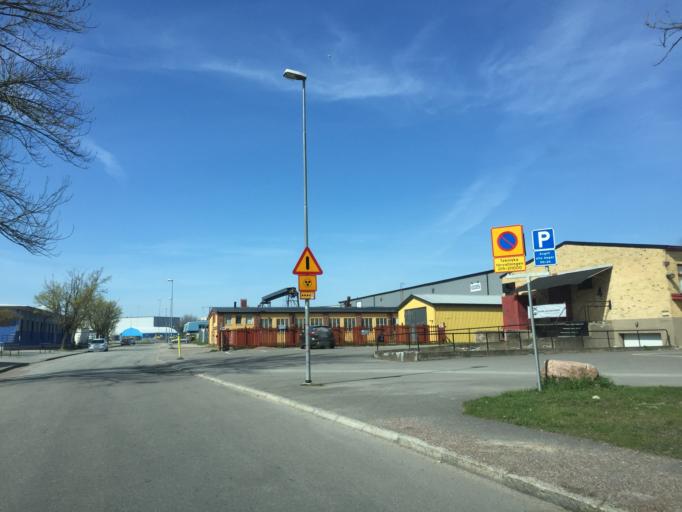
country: SE
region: OErebro
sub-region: Orebro Kommun
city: Orebro
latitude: 59.2605
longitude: 15.2096
